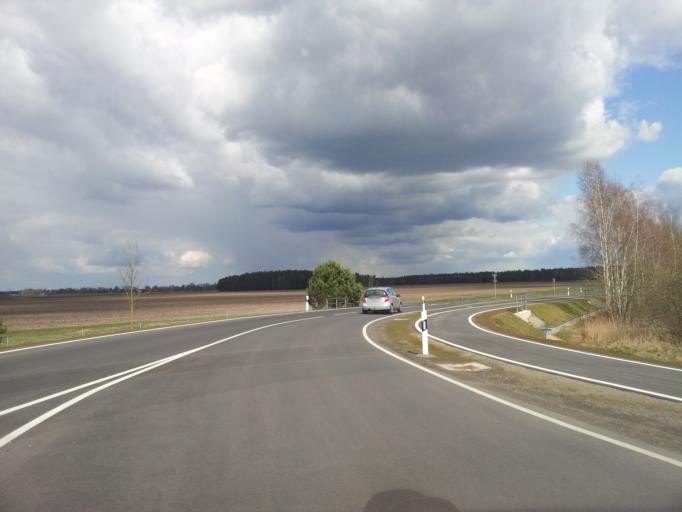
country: DE
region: Saxony
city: Wittichenau
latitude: 51.3843
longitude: 14.2598
